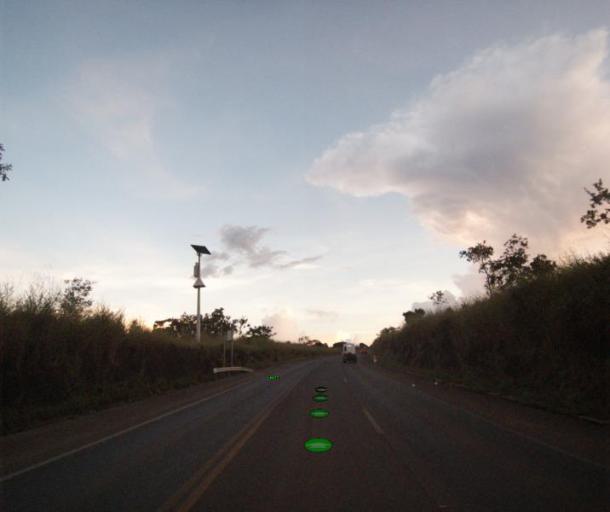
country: BR
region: Goias
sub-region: Uruacu
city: Uruacu
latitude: -14.5076
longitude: -49.1483
